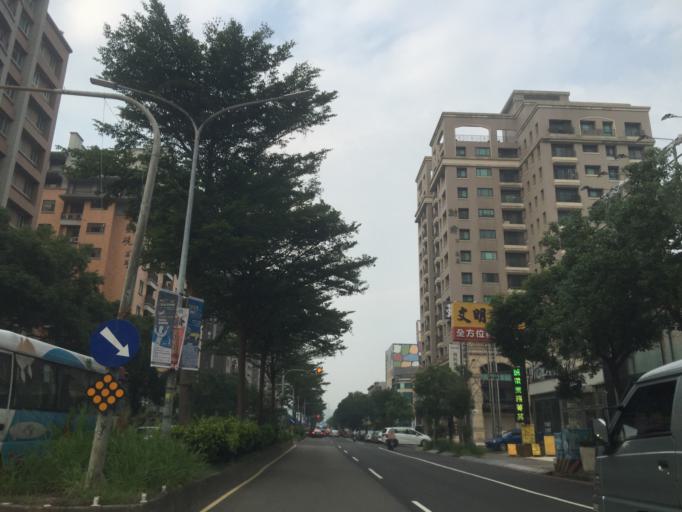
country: TW
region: Taiwan
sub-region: Hsinchu
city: Zhubei
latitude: 24.8318
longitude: 121.0185
